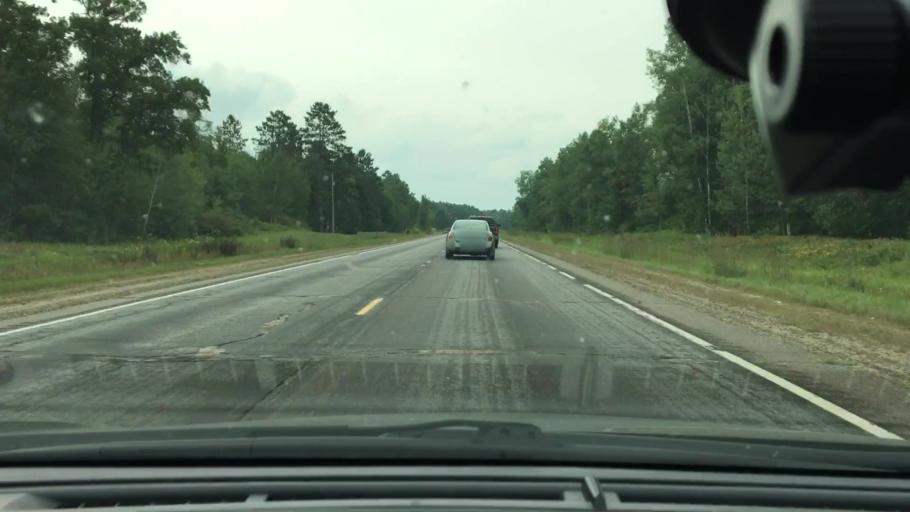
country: US
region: Minnesota
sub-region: Crow Wing County
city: Cross Lake
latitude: 46.6759
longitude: -93.9524
